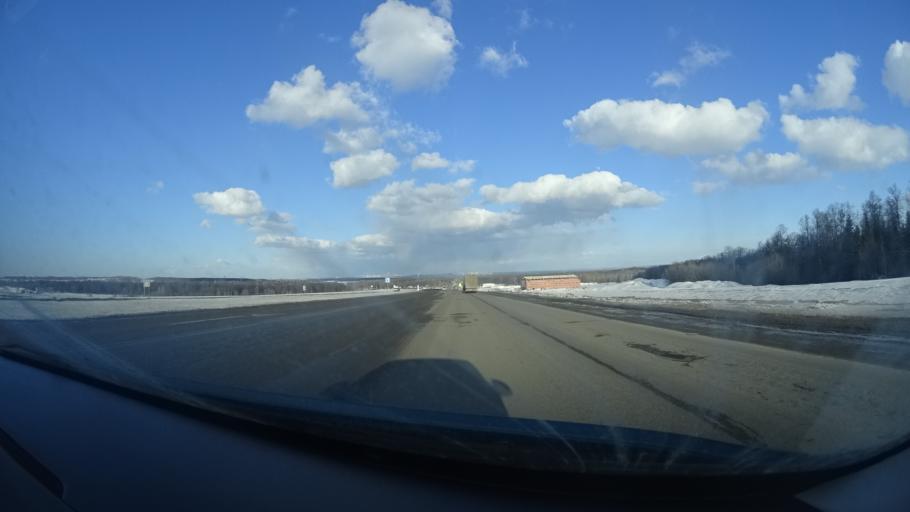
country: RU
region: Bashkortostan
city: Avdon
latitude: 54.6550
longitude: 55.6843
